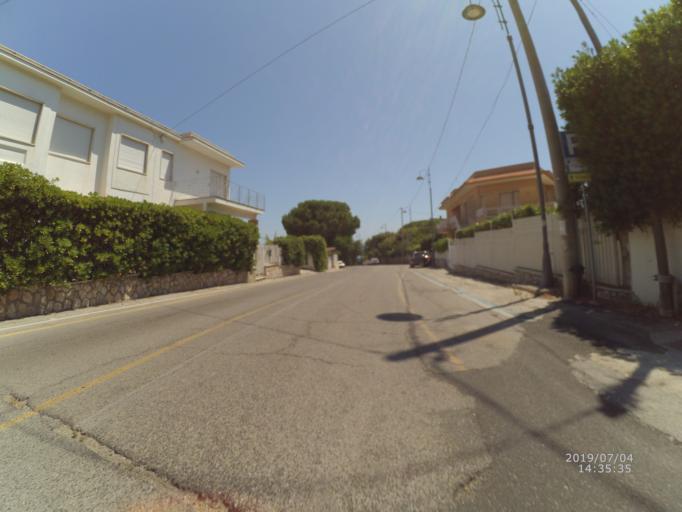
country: IT
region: Latium
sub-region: Provincia di Latina
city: Gaeta
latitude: 41.2086
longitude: 13.5504
